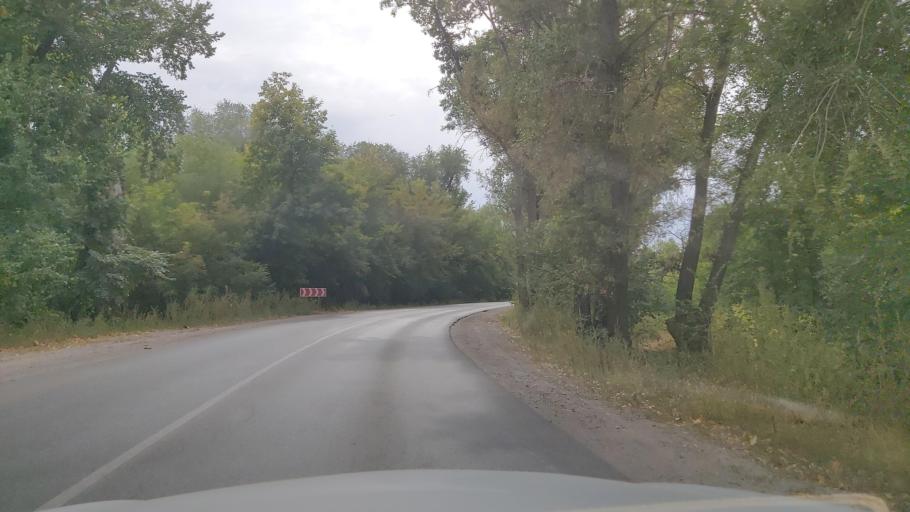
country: KZ
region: Almaty Oblysy
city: Energeticheskiy
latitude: 43.4049
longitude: 77.0525
